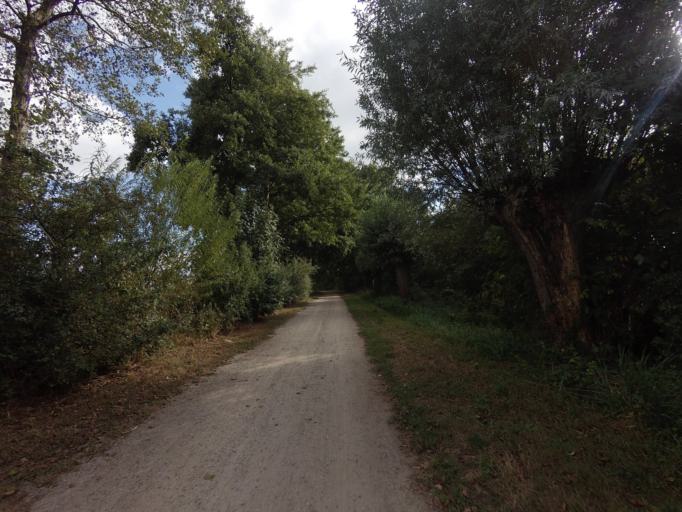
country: NL
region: North Brabant
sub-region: Gemeente Grave
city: Grave
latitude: 51.7474
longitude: 5.7369
